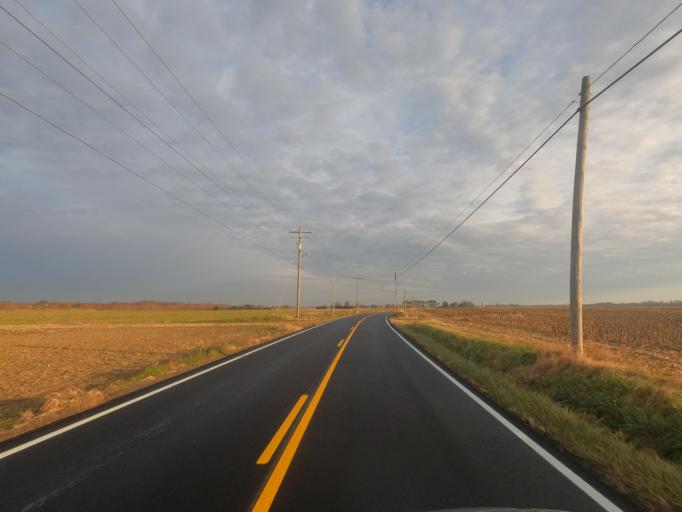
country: US
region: Delaware
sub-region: New Castle County
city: Townsend
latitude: 39.2853
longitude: -75.8358
